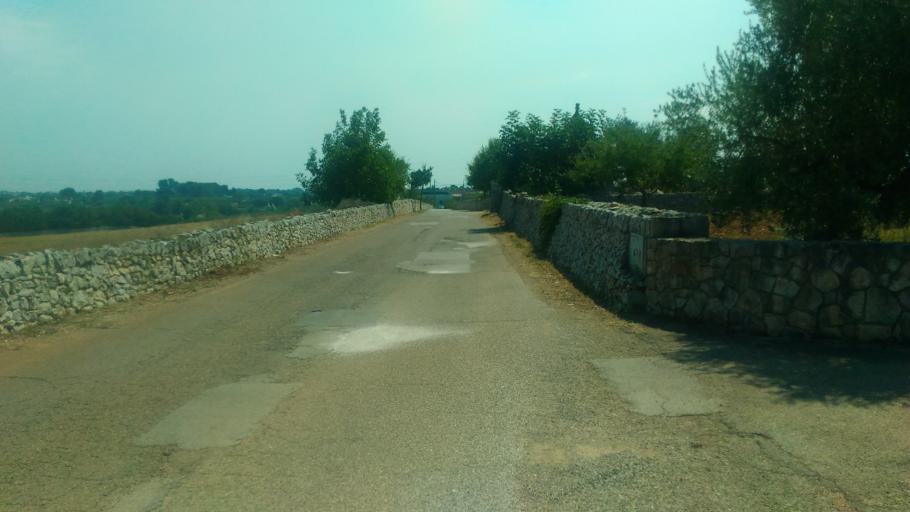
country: IT
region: Apulia
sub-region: Provincia di Brindisi
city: Cisternino
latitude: 40.7454
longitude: 17.3783
